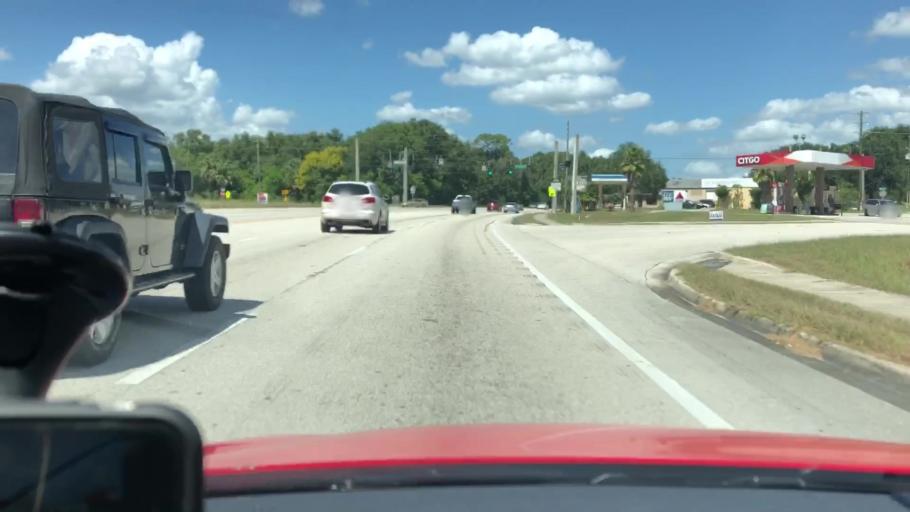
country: US
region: Florida
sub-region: Volusia County
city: West DeLand
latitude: 29.0125
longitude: -81.3227
